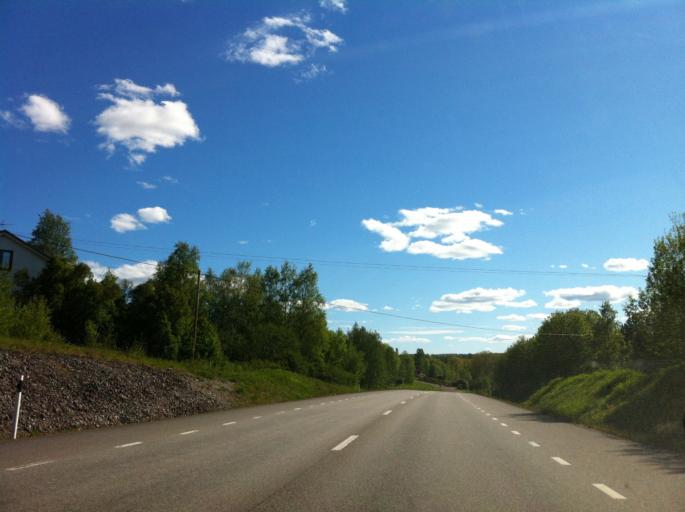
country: SE
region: Dalarna
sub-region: Rattviks Kommun
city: Raettvik
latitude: 60.8453
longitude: 15.1045
